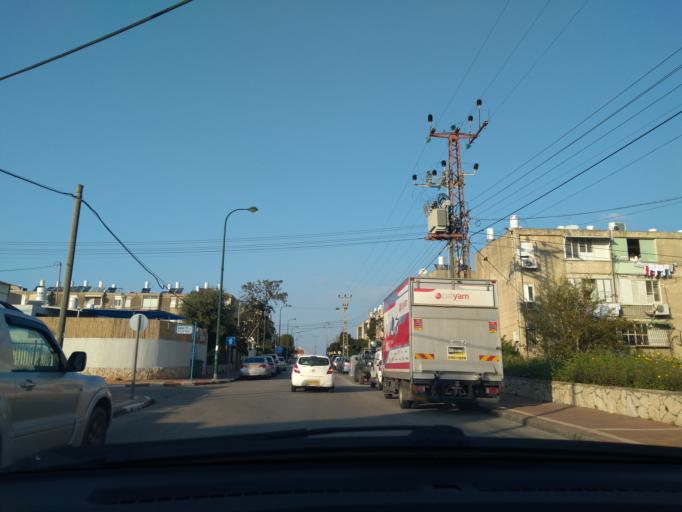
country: IL
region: Central District
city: Even Yehuda
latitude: 32.2801
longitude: 34.8557
